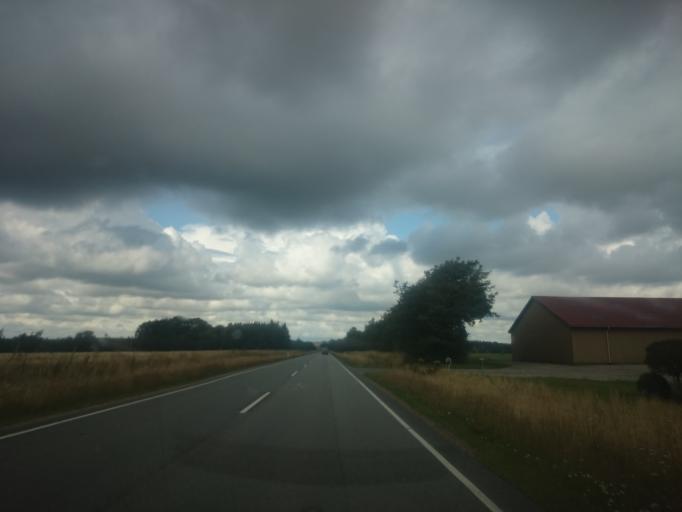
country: DK
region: South Denmark
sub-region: Billund Kommune
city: Grindsted
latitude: 55.6854
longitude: 8.9646
